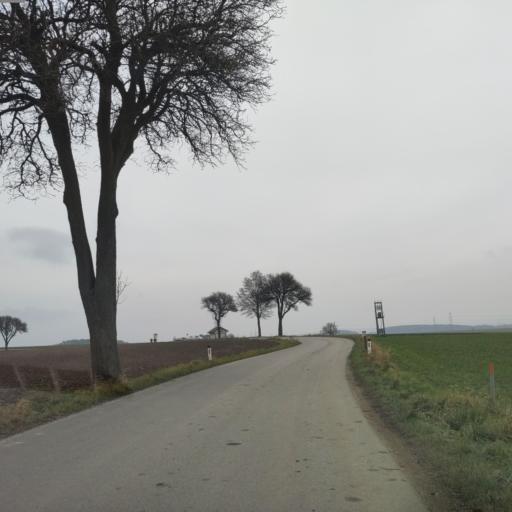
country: AT
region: Lower Austria
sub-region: Politischer Bezirk Sankt Polten
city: Karlstetten
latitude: 48.2465
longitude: 15.5579
